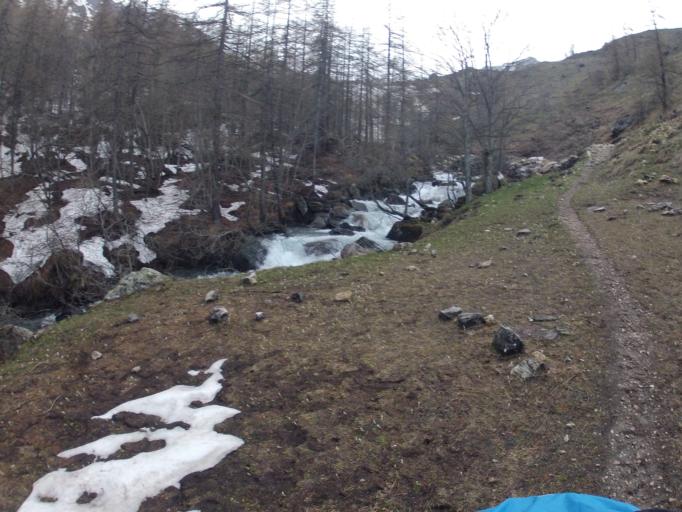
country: IT
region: Piedmont
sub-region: Provincia di Cuneo
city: Crissolo
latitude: 44.7002
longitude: 7.1288
